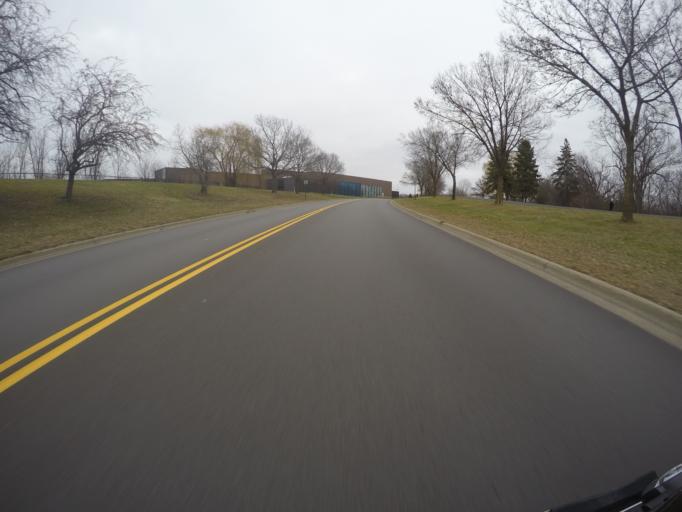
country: US
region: Minnesota
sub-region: Hennepin County
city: Eden Prairie
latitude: 44.8706
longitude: -93.4919
